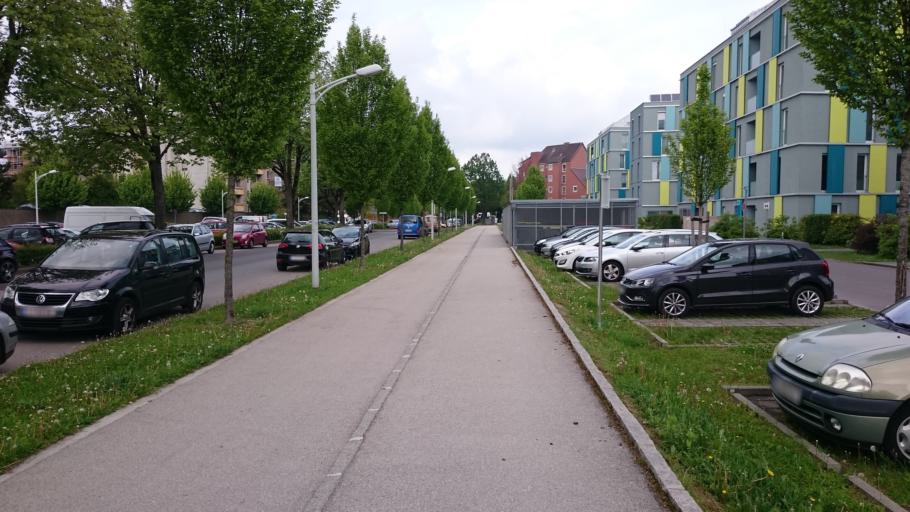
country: AT
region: Upper Austria
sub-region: Politischer Bezirk Linz-Land
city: Leonding
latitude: 48.2633
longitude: 14.2809
